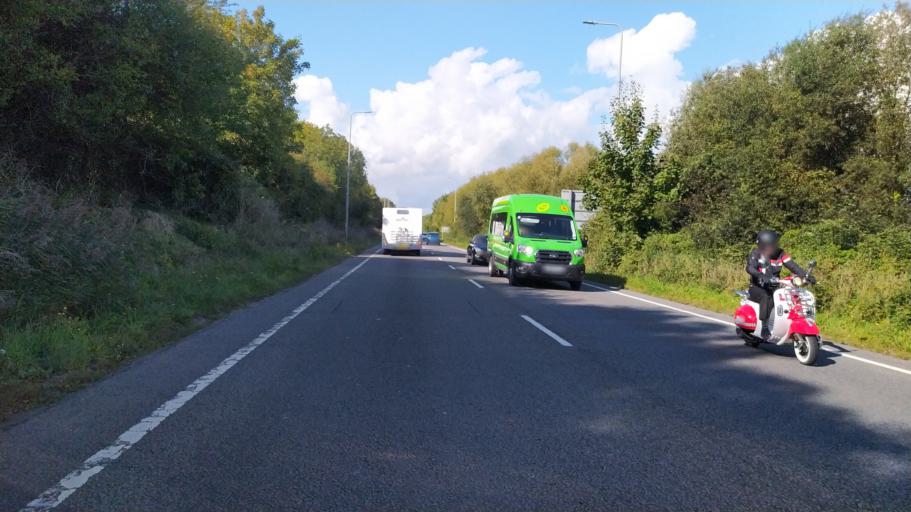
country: GB
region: England
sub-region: Dorset
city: Weymouth
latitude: 50.6229
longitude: -2.4699
